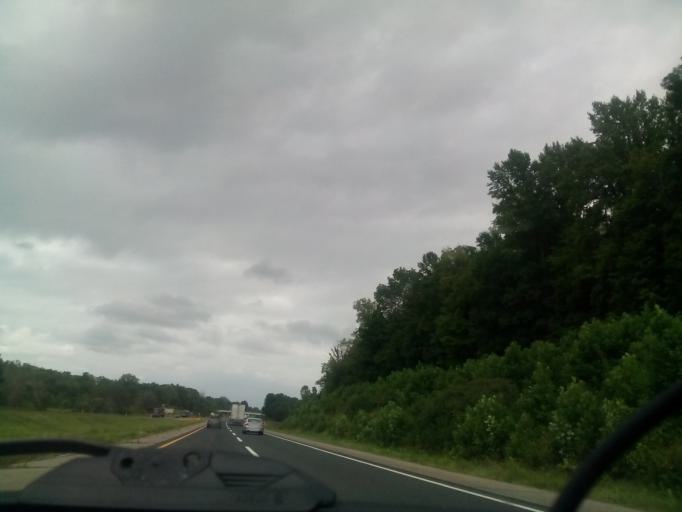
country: US
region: Indiana
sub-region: Steuben County
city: Fremont
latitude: 41.6441
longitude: -84.8370
